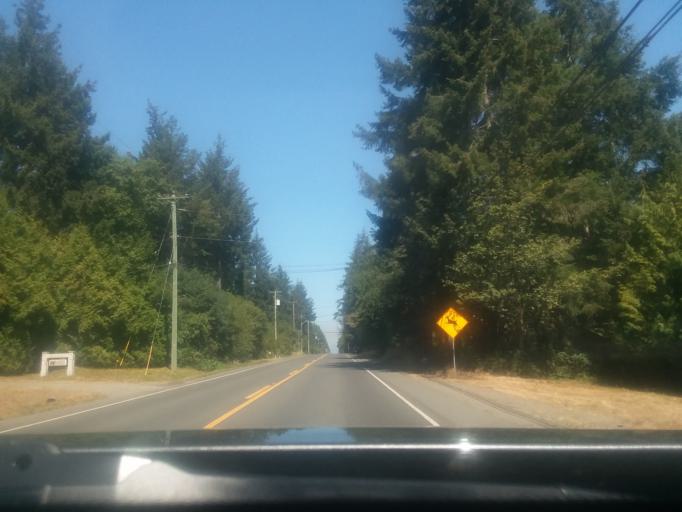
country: CA
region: British Columbia
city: Courtenay
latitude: 49.7049
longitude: -124.9341
